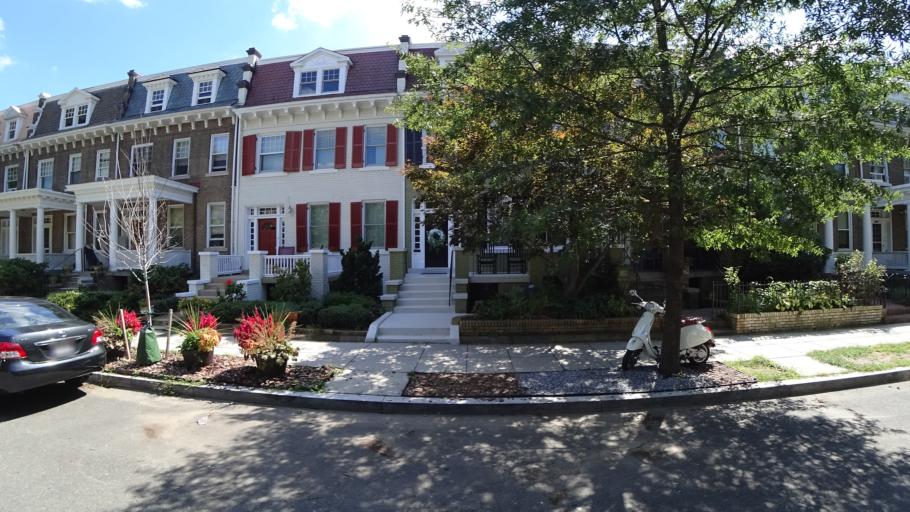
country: US
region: Washington, D.C.
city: Washington, D.C.
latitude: 38.9279
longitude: -77.0394
